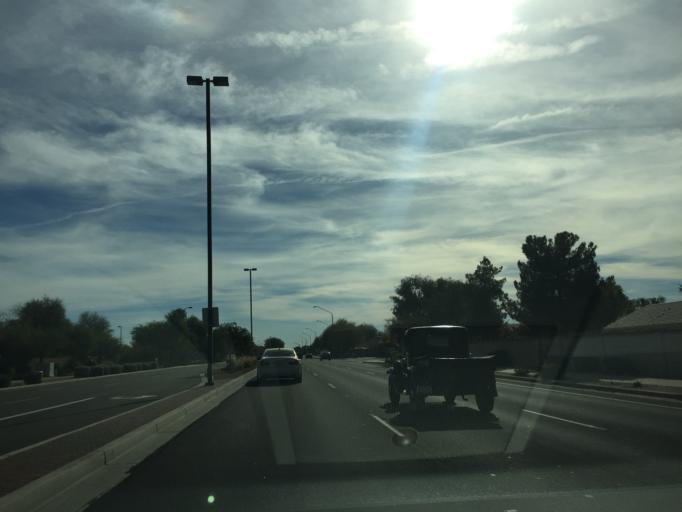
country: US
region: Arizona
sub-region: Maricopa County
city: Chandler
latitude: 33.3001
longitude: -111.7897
